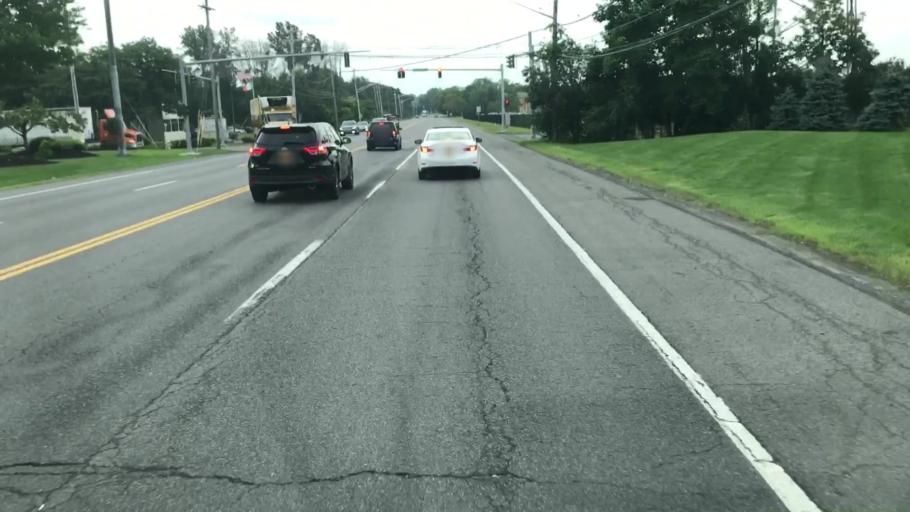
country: US
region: New York
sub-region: Onondaga County
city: Galeville
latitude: 43.1146
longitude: -76.1851
